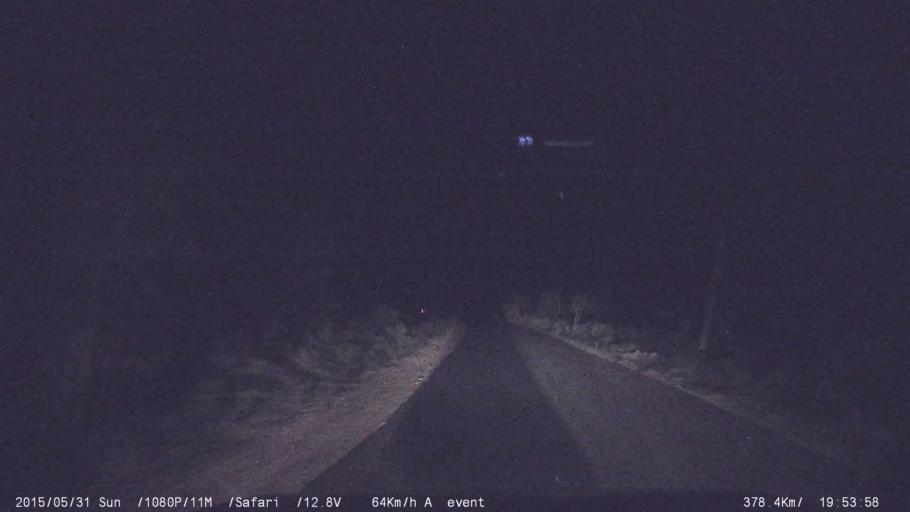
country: IN
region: Karnataka
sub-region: Mandya
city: Malavalli
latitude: 12.3507
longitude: 77.0744
